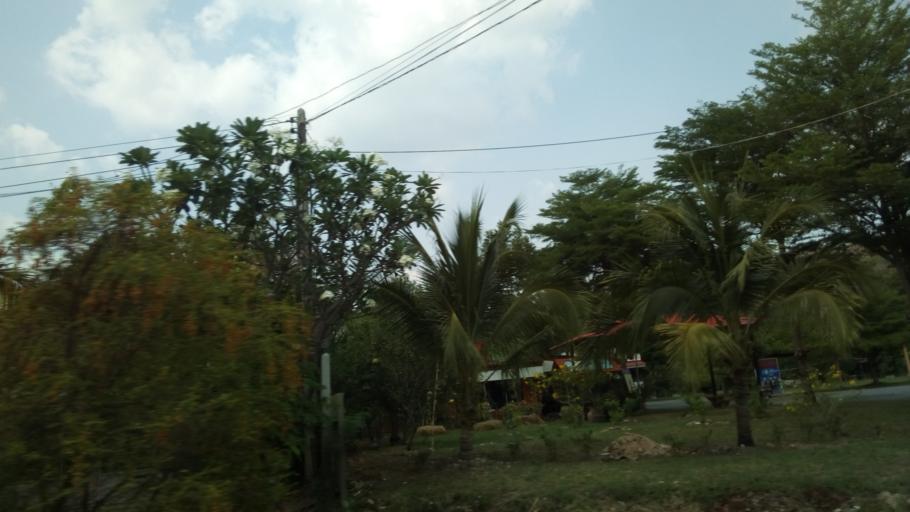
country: TH
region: Sara Buri
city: Saraburi
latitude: 14.4622
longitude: 100.9426
